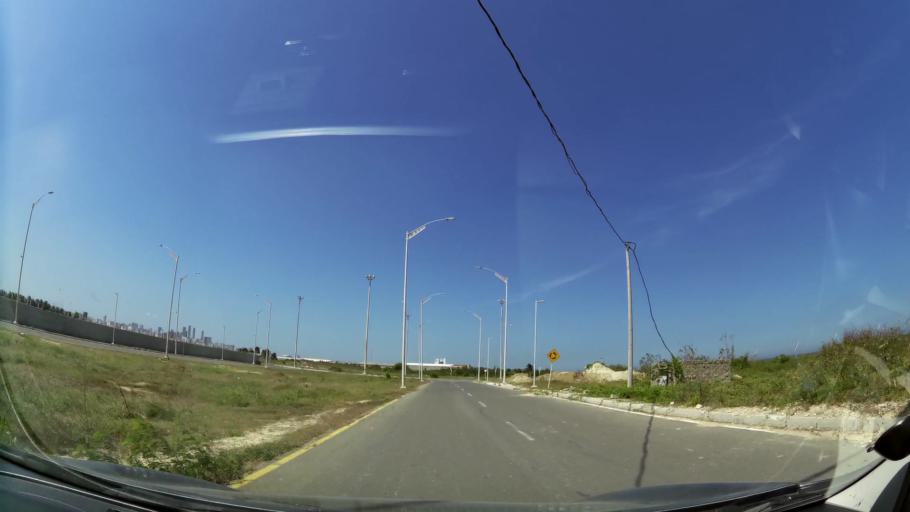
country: CO
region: Atlantico
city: Barranquilla
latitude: 10.9975
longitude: -74.7718
